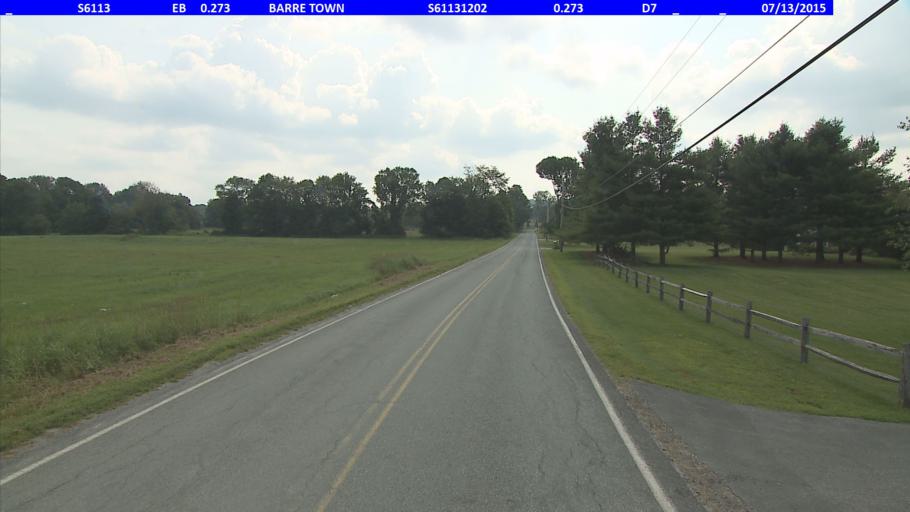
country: US
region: Vermont
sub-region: Washington County
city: Barre
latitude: 44.2205
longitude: -72.4670
